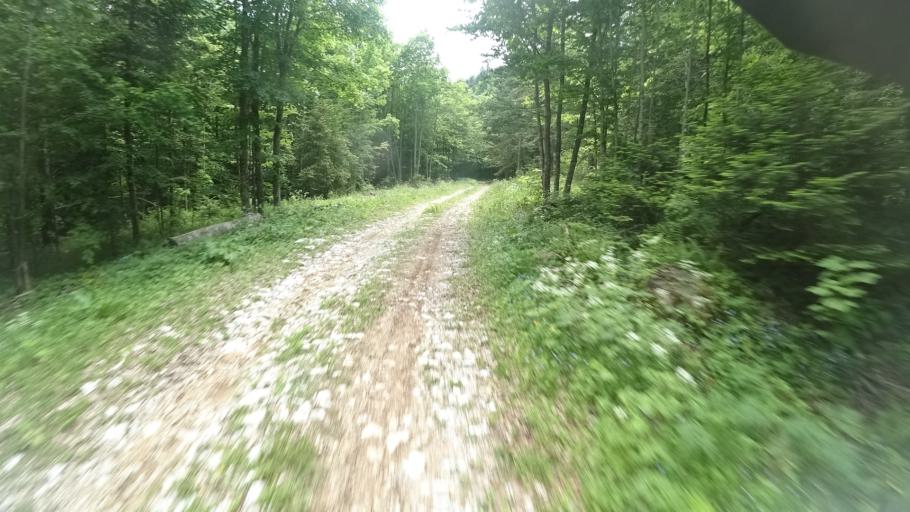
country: HR
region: Zadarska
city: Gracac
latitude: 44.4796
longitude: 15.8828
